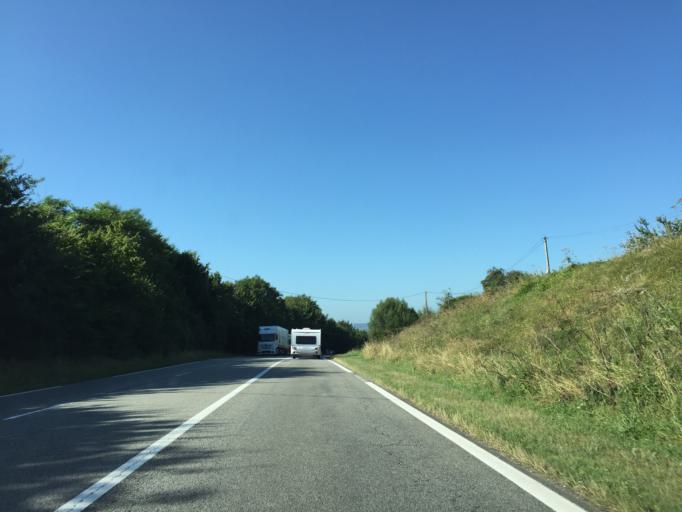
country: FR
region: Lower Normandy
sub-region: Departement du Calvados
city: Lisieux
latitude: 49.1961
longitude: 0.2273
